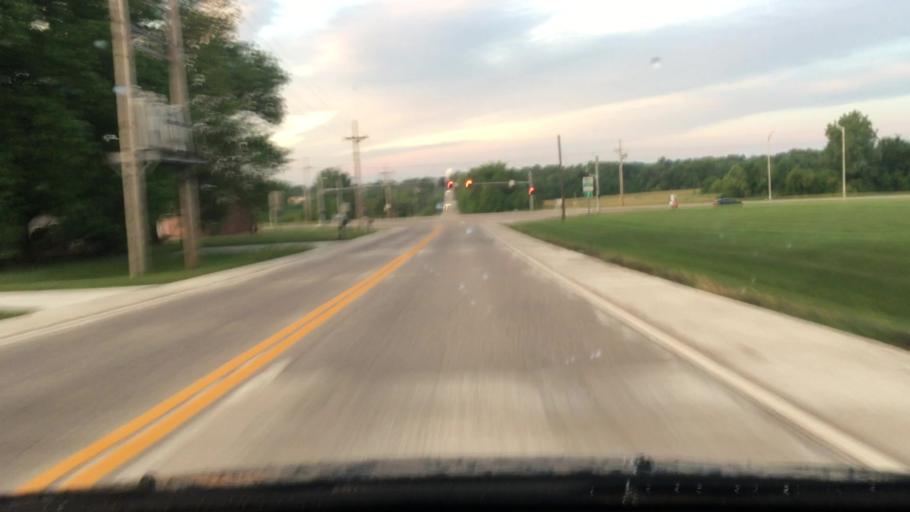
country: US
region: Missouri
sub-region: Cass County
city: Lake Winnebago
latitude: 38.8551
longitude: -94.4172
